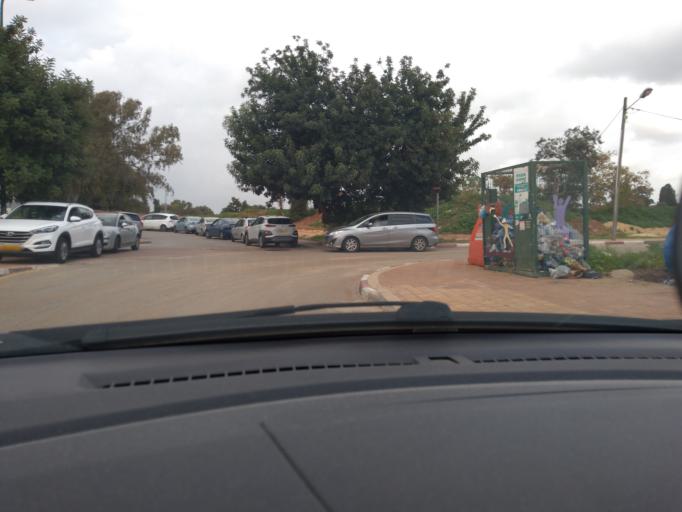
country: IL
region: Central District
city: Netanya
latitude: 32.3456
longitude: 34.8625
